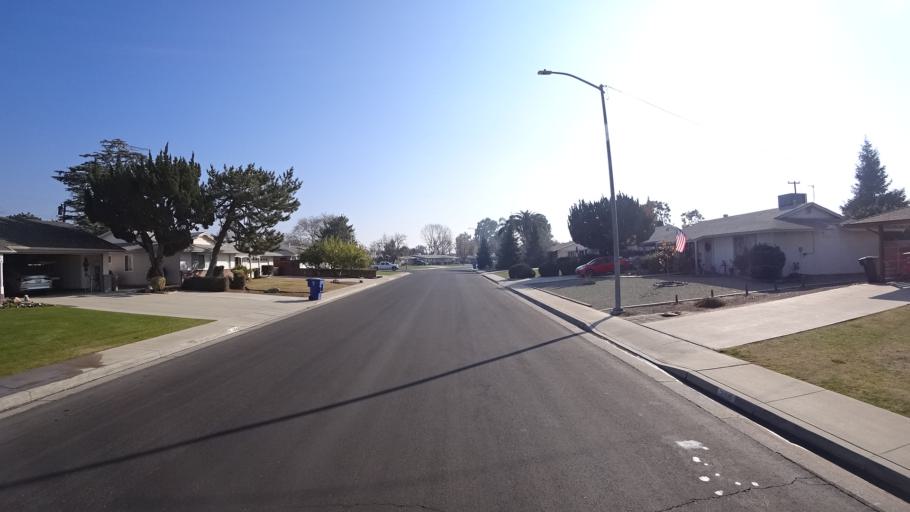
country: US
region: California
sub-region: Kern County
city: Greenacres
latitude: 35.3487
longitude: -119.0716
